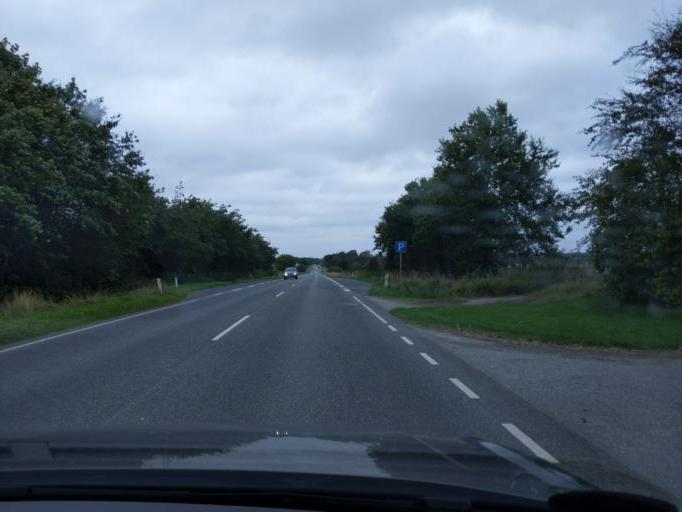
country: DK
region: North Denmark
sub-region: Mariagerfjord Kommune
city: Mariager
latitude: 56.5365
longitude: 9.9025
